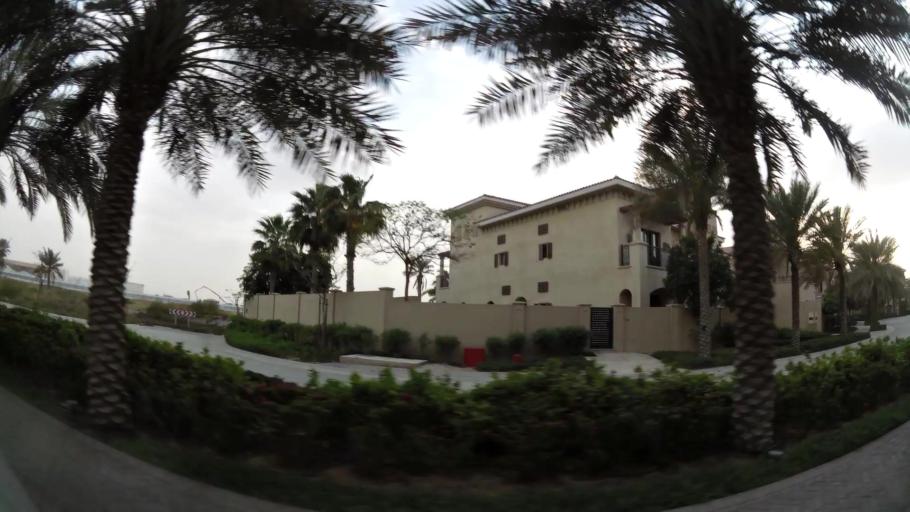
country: AE
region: Abu Dhabi
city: Abu Dhabi
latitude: 24.5371
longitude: 54.4257
